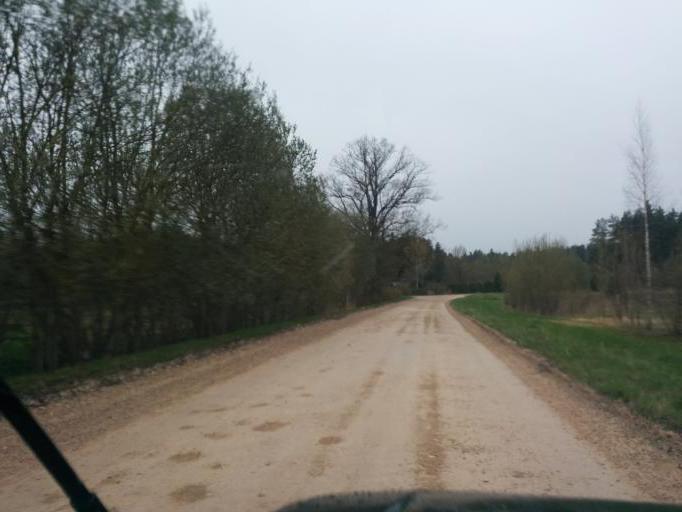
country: LV
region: Lecava
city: Iecava
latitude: 56.6150
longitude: 24.1760
